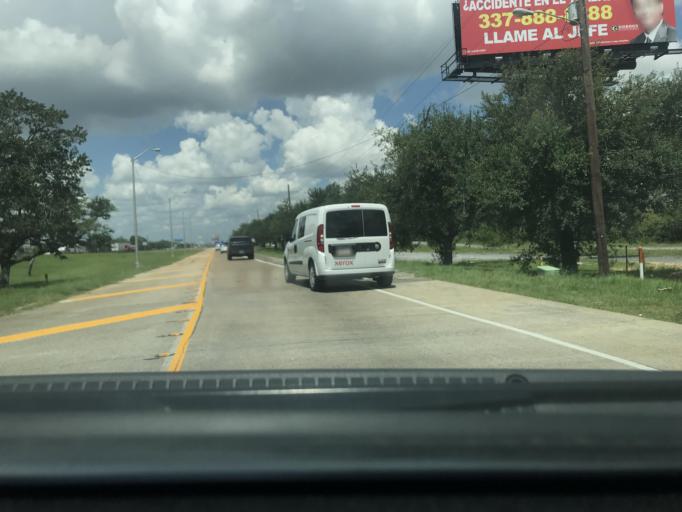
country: US
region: Louisiana
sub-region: Calcasieu Parish
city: Westlake
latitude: 30.2373
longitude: -93.2216
